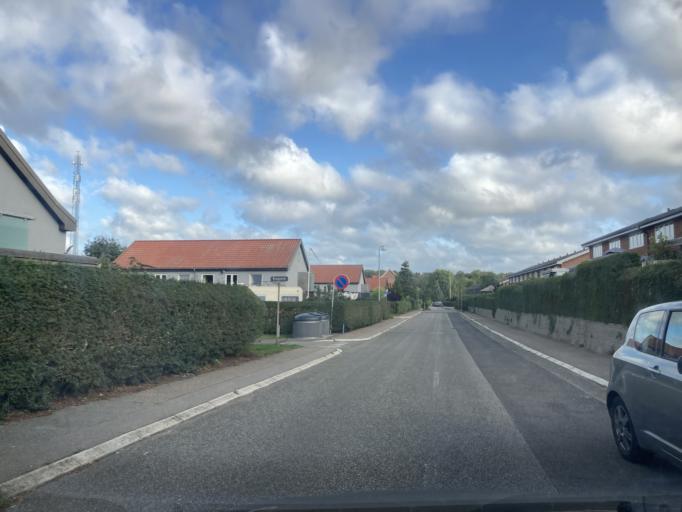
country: DK
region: Capital Region
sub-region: Halsnaes Kommune
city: Frederiksvaerk
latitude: 55.9781
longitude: 12.0259
